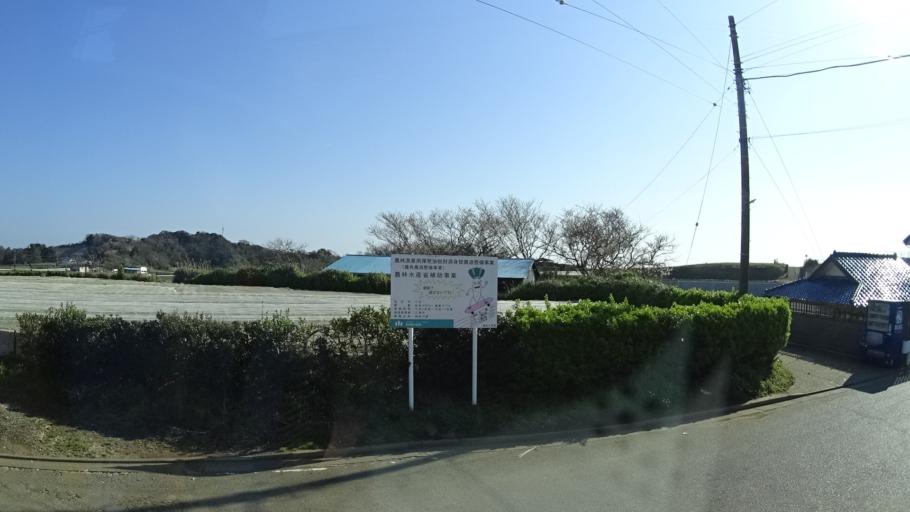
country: JP
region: Kanagawa
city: Miura
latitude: 35.1567
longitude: 139.6439
